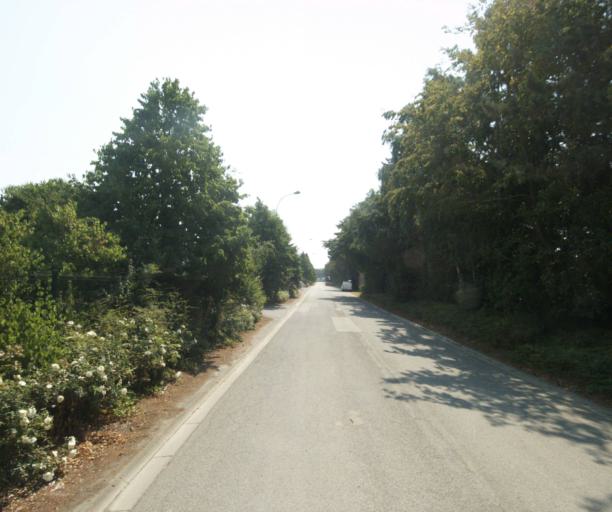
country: FR
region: Nord-Pas-de-Calais
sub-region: Departement du Nord
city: Wambrechies
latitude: 50.6935
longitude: 3.0275
